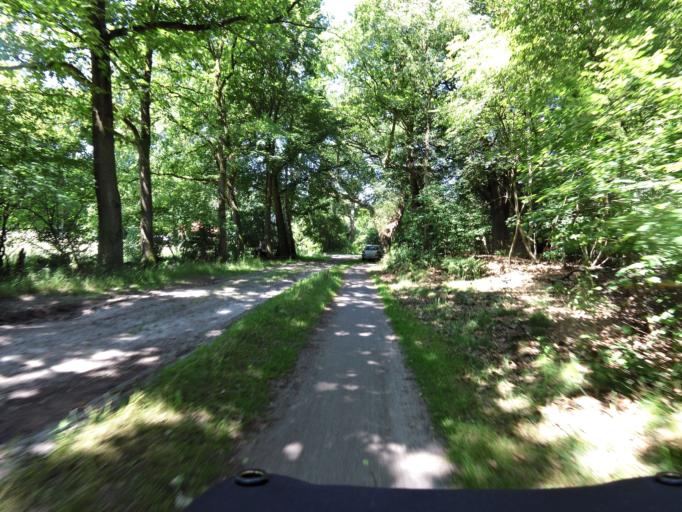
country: NL
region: Overijssel
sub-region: Gemeente Twenterand
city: Den Ham
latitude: 52.4891
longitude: 6.4573
